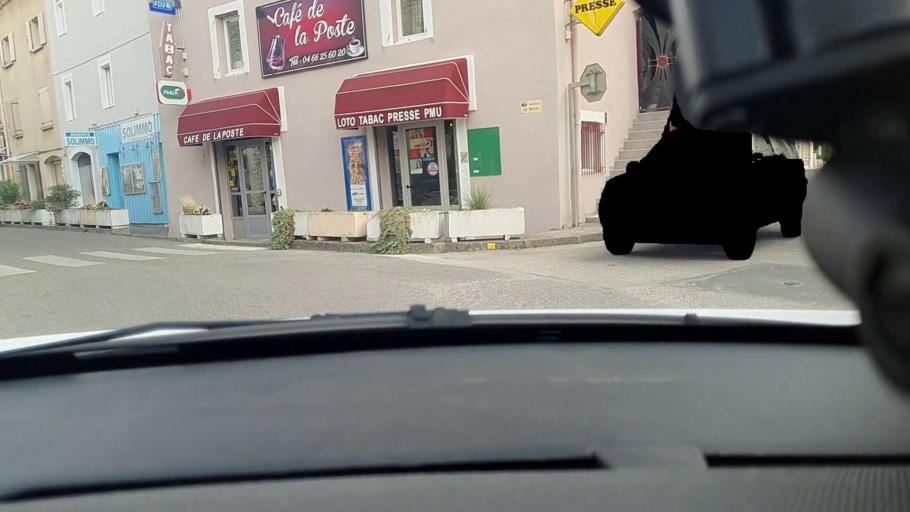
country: FR
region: Languedoc-Roussillon
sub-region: Departement du Gard
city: Les Mages
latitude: 44.2287
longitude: 4.1662
